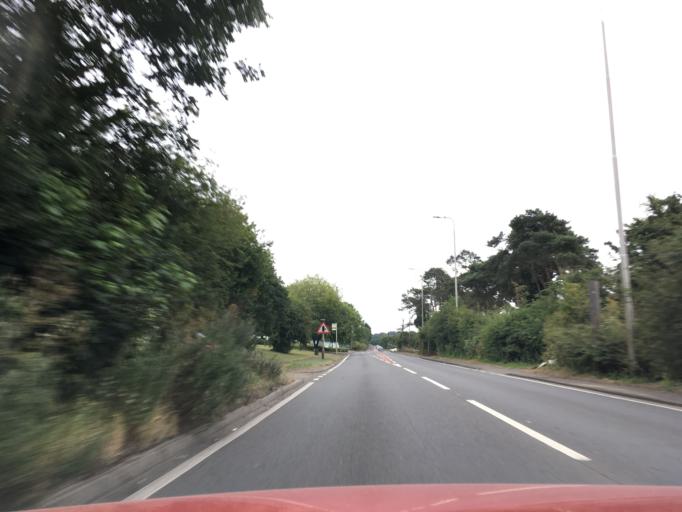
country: GB
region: England
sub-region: Hertfordshire
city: Flamstead
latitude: 51.8293
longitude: -0.4463
